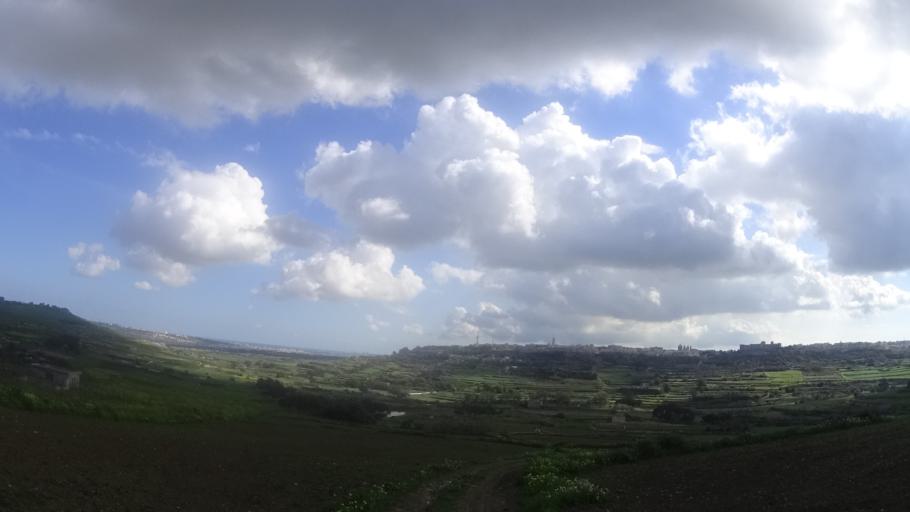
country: MT
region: L-Imtarfa
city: Imtarfa
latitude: 35.8989
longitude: 14.3863
